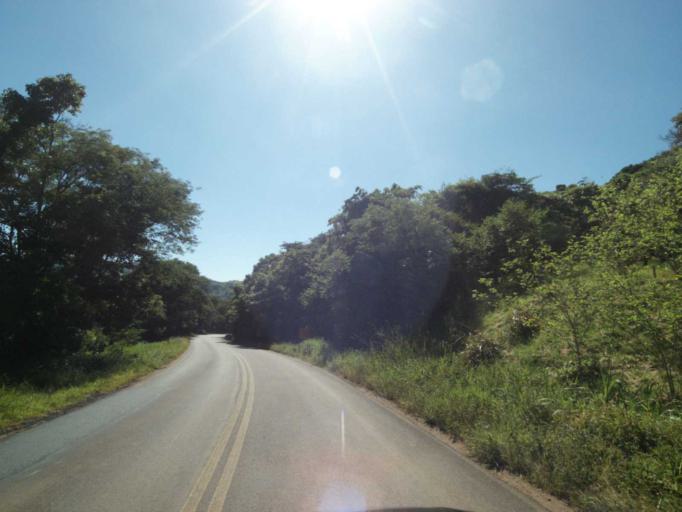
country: BR
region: Parana
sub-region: Francisco Beltrao
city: Francisco Beltrao
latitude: -26.1458
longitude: -53.3190
